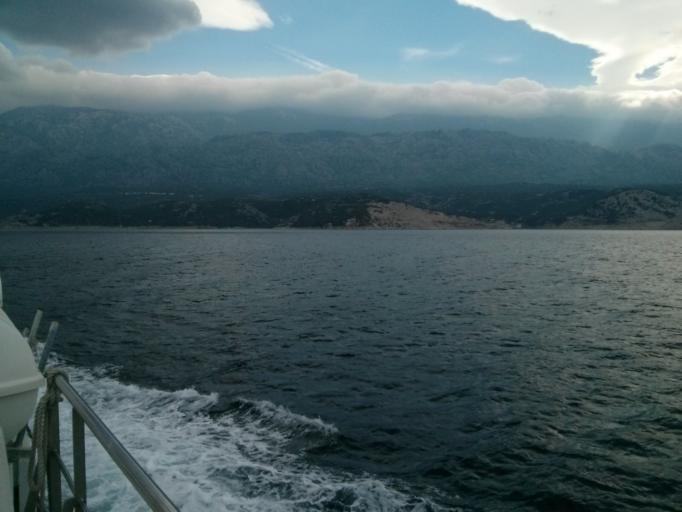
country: HR
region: Primorsko-Goranska
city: Banjol
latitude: 44.7057
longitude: 14.8727
